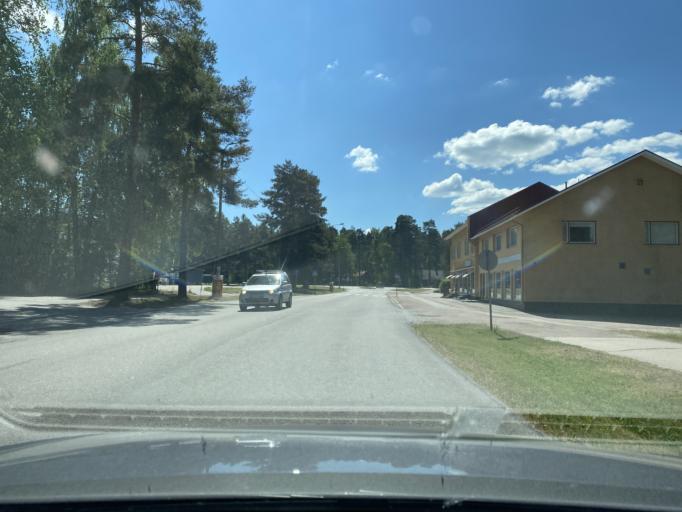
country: FI
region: Satakunta
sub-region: Rauma
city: Eura
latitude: 61.1170
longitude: 22.1611
